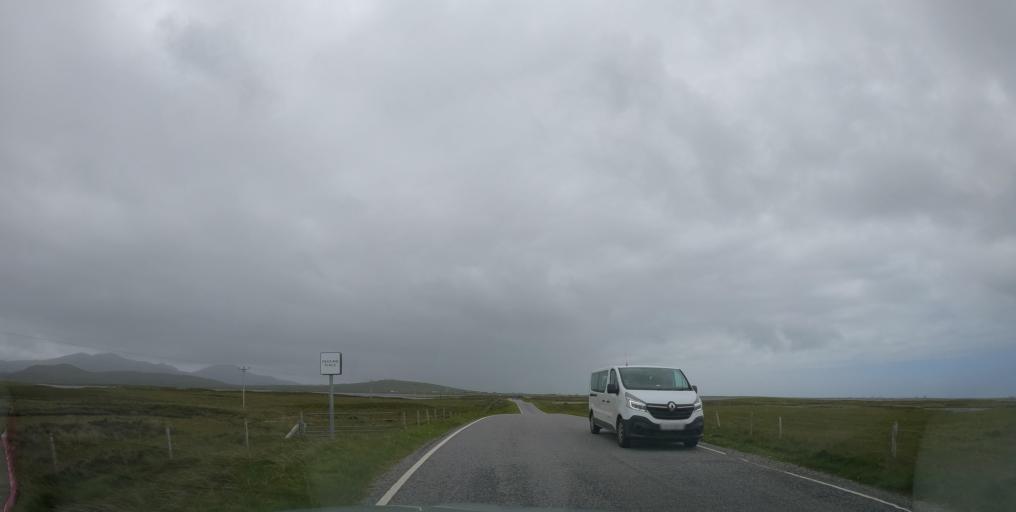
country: GB
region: Scotland
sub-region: Eilean Siar
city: Benbecula
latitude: 57.3686
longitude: -7.3503
